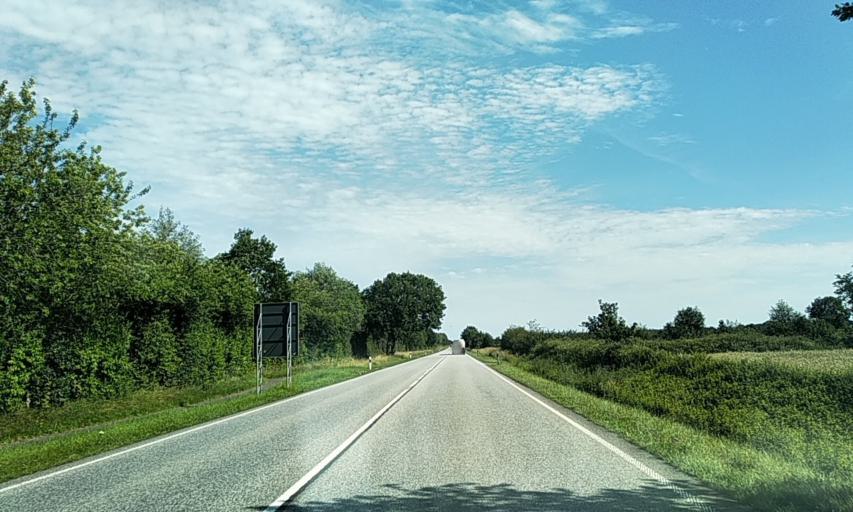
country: DE
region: Schleswig-Holstein
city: Kropp
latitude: 54.4201
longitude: 9.5302
